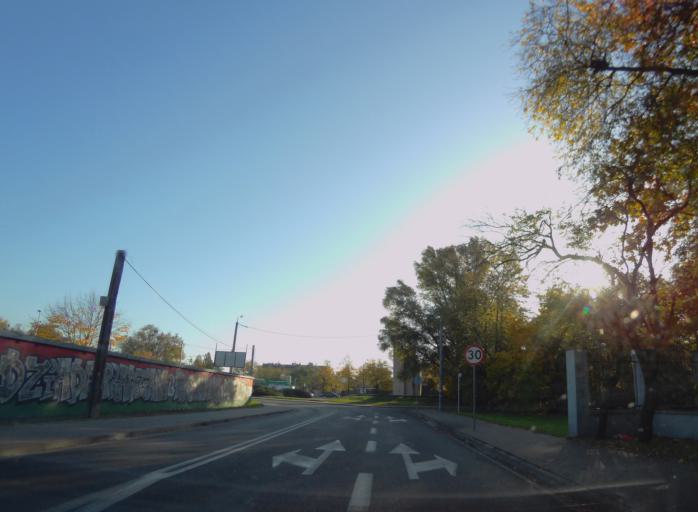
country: PL
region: Masovian Voivodeship
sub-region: Powiat pruszkowski
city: Granica
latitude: 52.1522
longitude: 20.7883
